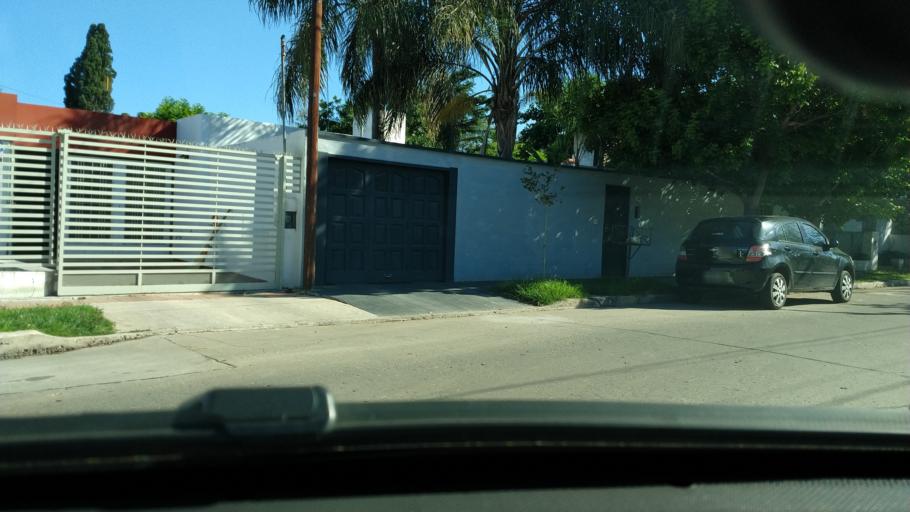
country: AR
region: Cordoba
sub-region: Departamento de Capital
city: Cordoba
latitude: -31.3662
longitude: -64.2278
